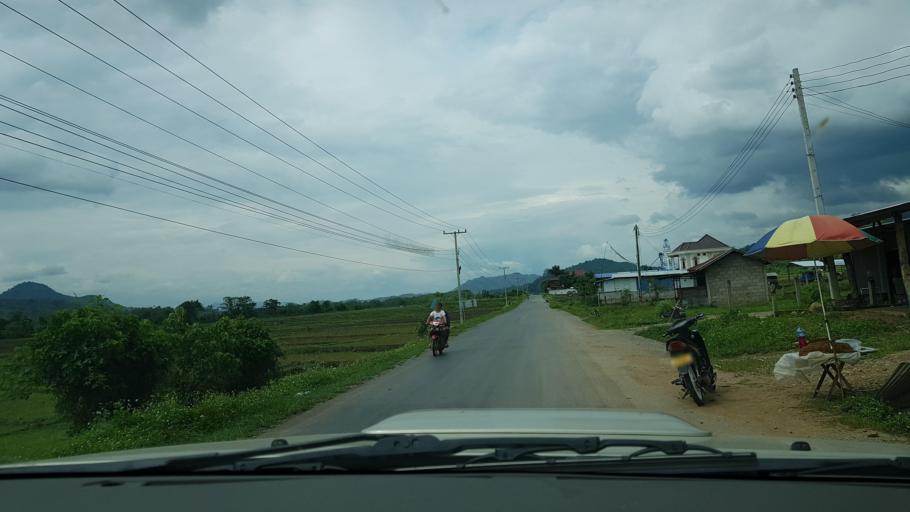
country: LA
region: Loungnamtha
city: Muang Nale
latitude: 20.3221
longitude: 101.6615
